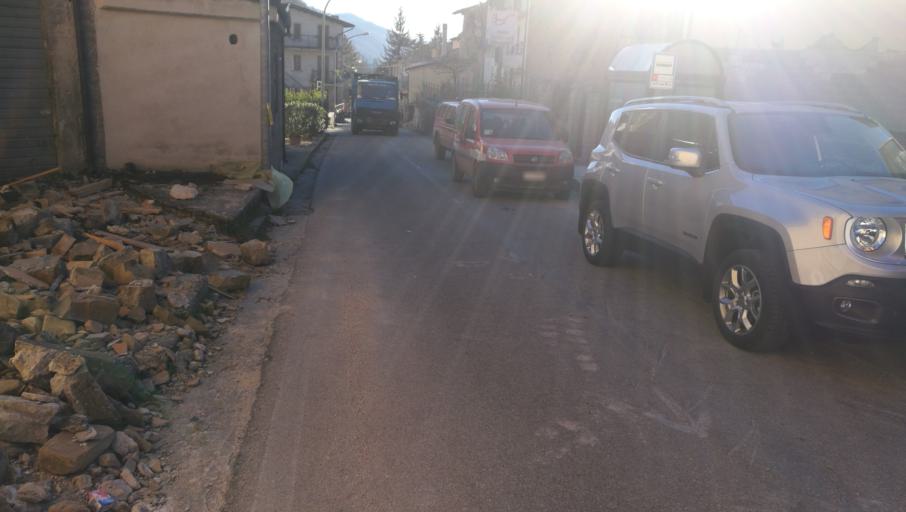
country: IT
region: The Marches
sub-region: Provincia di Ascoli Piceno
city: Arquata del Tronto
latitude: 42.7893
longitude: 13.3009
